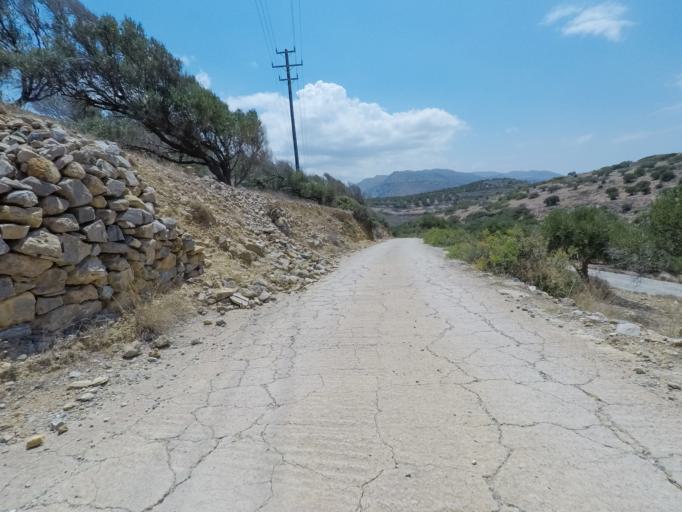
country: GR
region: Crete
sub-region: Nomos Lasithiou
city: Elounda
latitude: 35.3195
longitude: 25.7494
